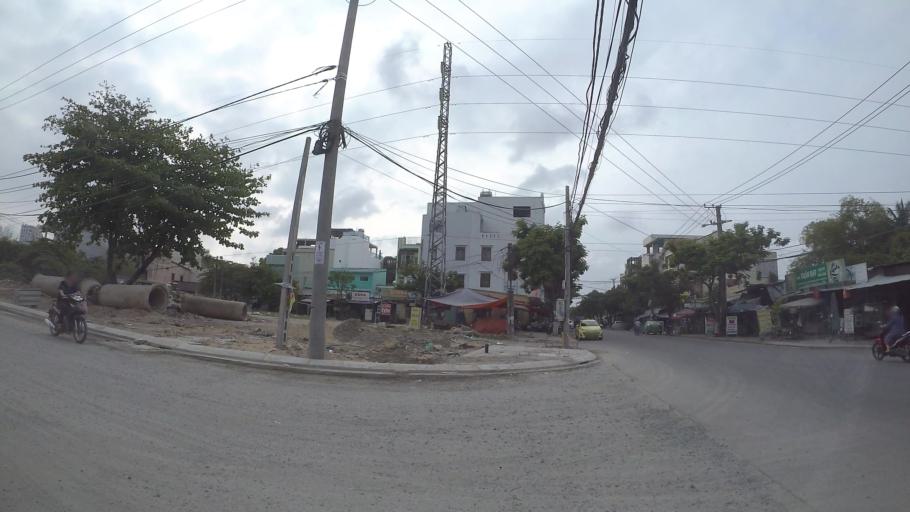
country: VN
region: Da Nang
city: Son Tra
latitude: 16.0655
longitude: 108.2398
